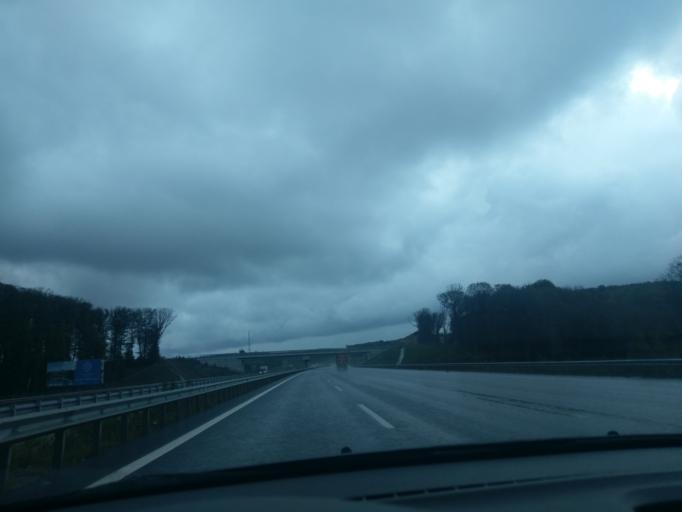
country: TR
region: Istanbul
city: Kemerburgaz
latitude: 41.2335
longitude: 28.9215
